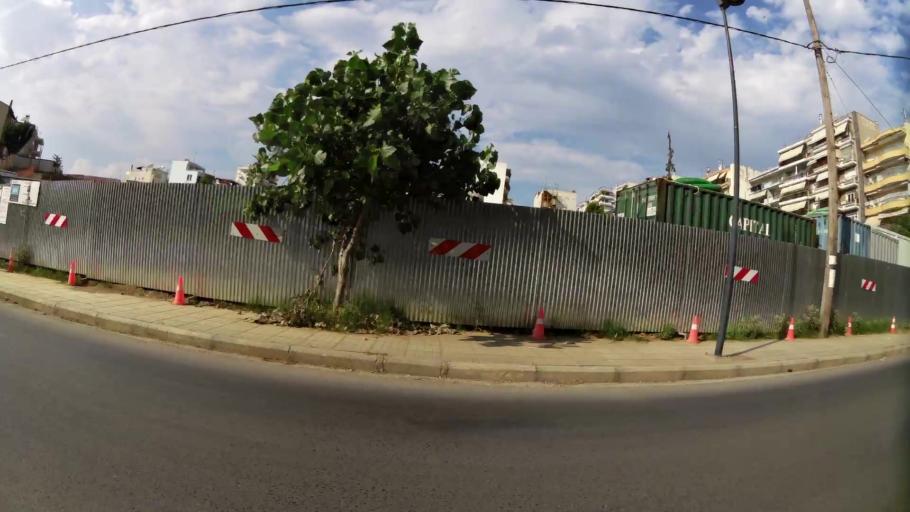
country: GR
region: Central Macedonia
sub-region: Nomos Thessalonikis
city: Polichni
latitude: 40.6589
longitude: 22.9545
